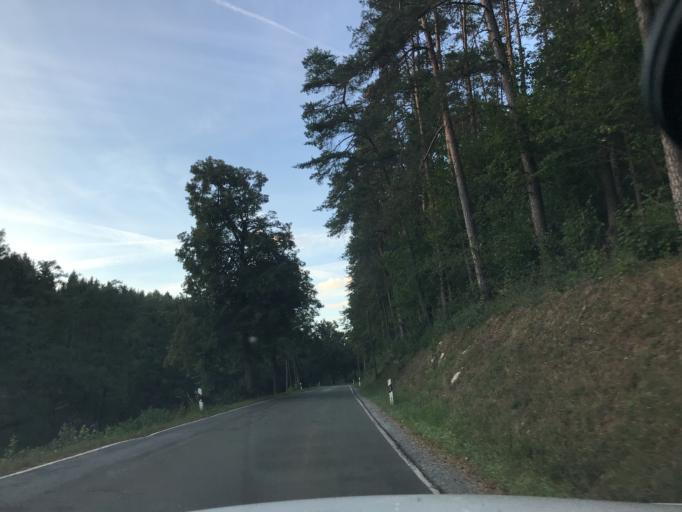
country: DE
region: Bavaria
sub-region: Upper Franconia
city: Pegnitz
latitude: 49.7371
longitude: 11.5523
